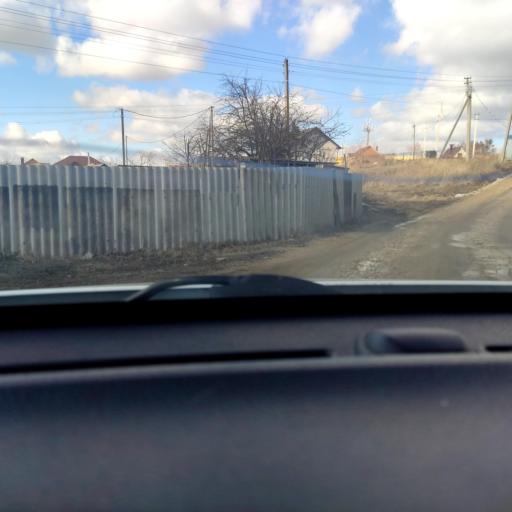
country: RU
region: Voronezj
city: Somovo
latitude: 51.6909
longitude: 39.3802
